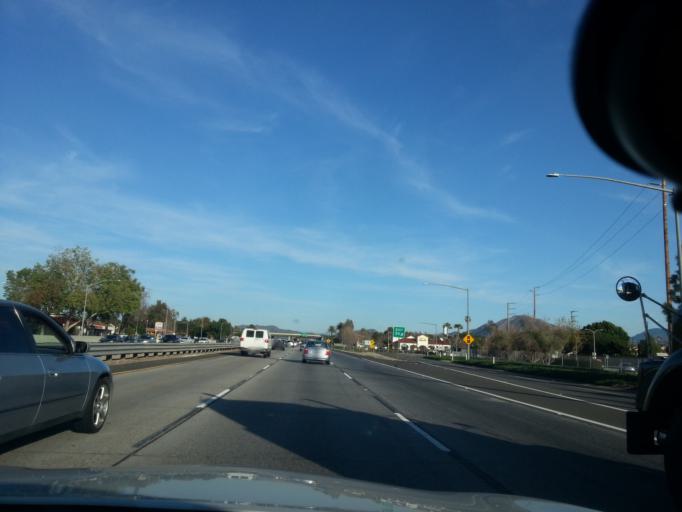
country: US
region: California
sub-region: Ventura County
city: Camarillo
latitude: 34.2180
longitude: -119.0560
